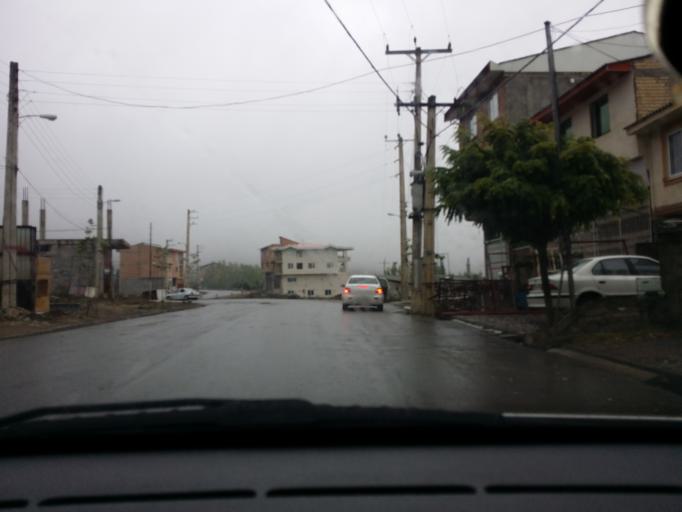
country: IR
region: Mazandaran
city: Chalus
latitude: 36.5244
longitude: 51.2329
